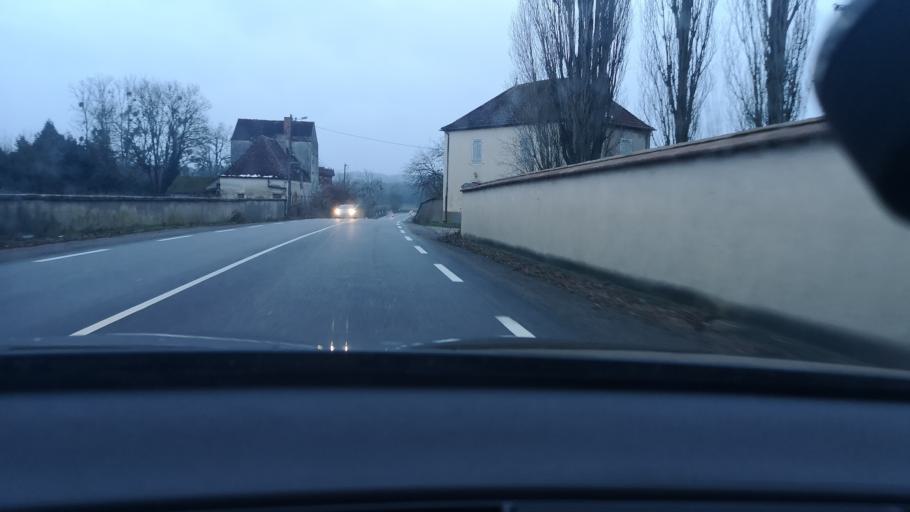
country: FR
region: Bourgogne
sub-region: Departement de la Cote-d'Or
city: Aiserey
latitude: 47.1278
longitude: 5.0967
